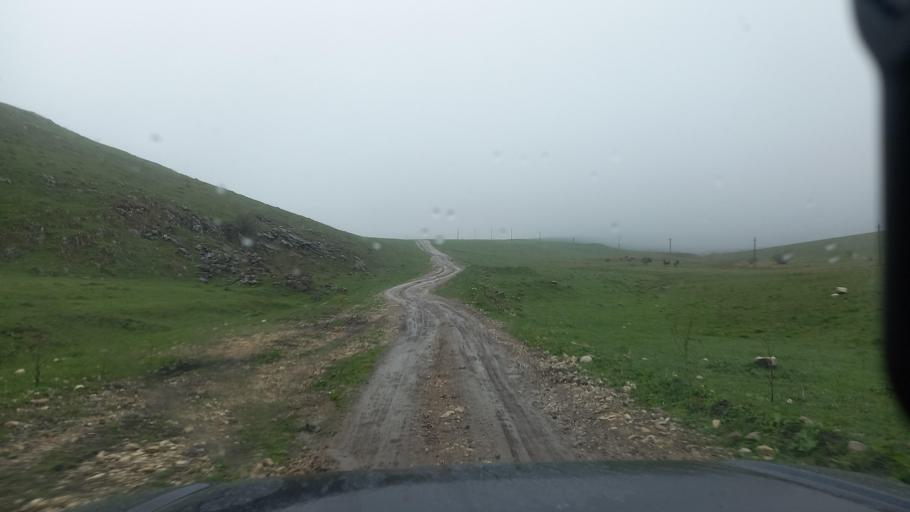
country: RU
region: Kabardino-Balkariya
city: Kamennomostskoye
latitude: 43.6181
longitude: 43.0164
